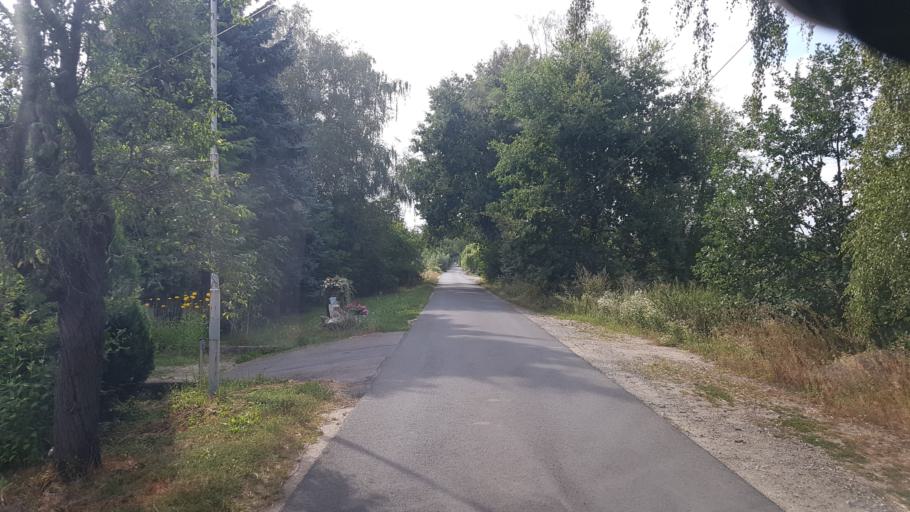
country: DE
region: Brandenburg
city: Plessa
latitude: 51.4419
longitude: 13.5927
